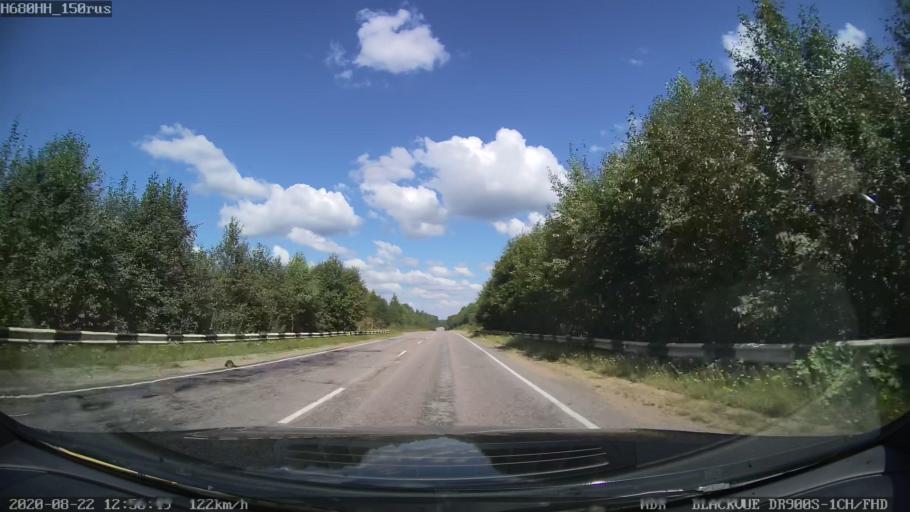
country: RU
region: Tverskaya
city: Rameshki
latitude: 57.5624
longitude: 36.3217
